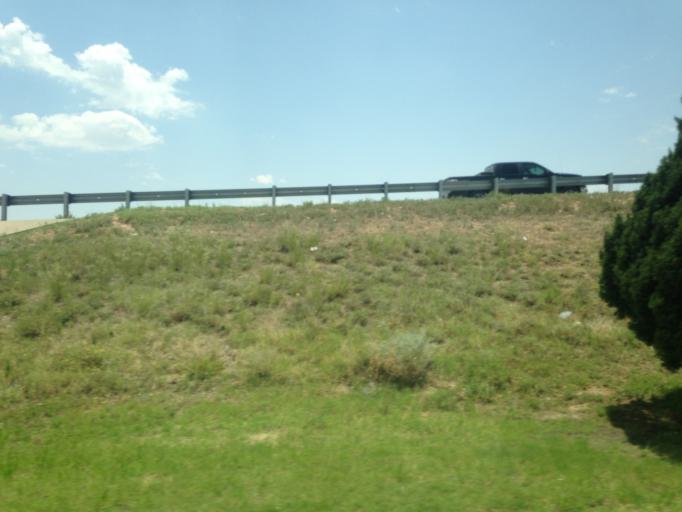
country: US
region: Texas
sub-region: Midland County
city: Midland
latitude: 32.0344
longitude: -102.1275
